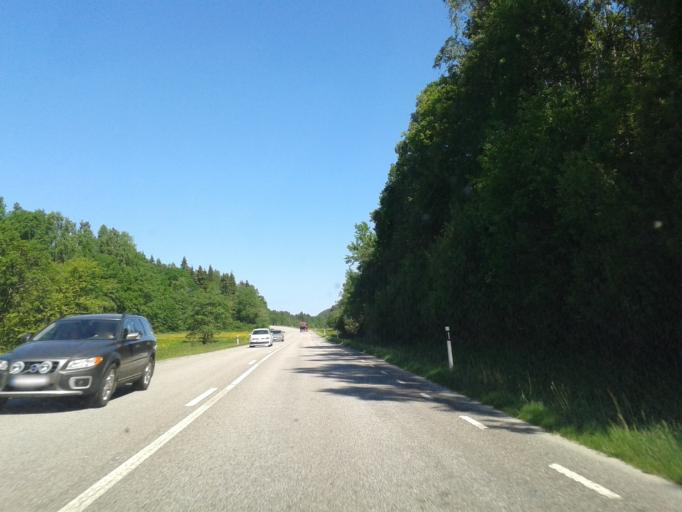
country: SE
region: Vaestra Goetaland
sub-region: Orust
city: Henan
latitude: 58.1851
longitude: 11.6933
